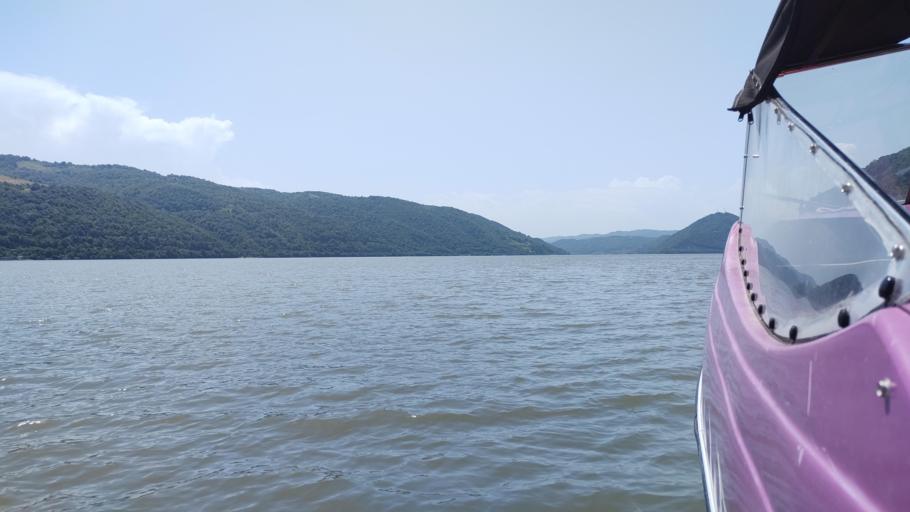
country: RO
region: Mehedinti
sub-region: Comuna Svinita
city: Svinita
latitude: 44.4977
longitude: 22.1888
